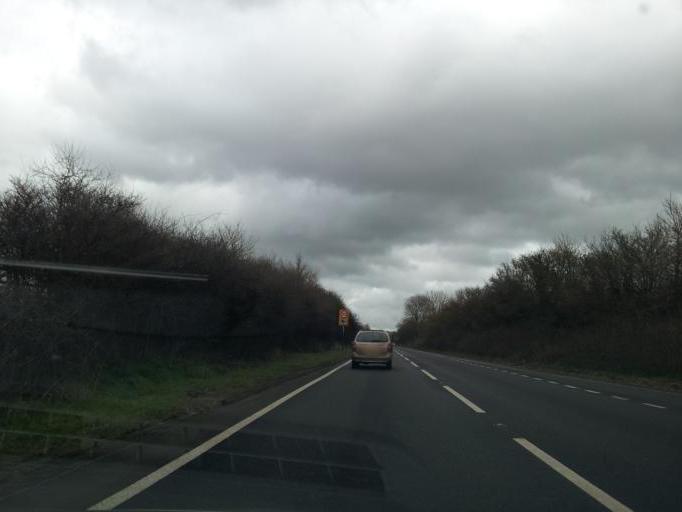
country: GB
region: England
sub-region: Somerset
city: Ilchester
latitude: 51.0225
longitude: -2.6359
